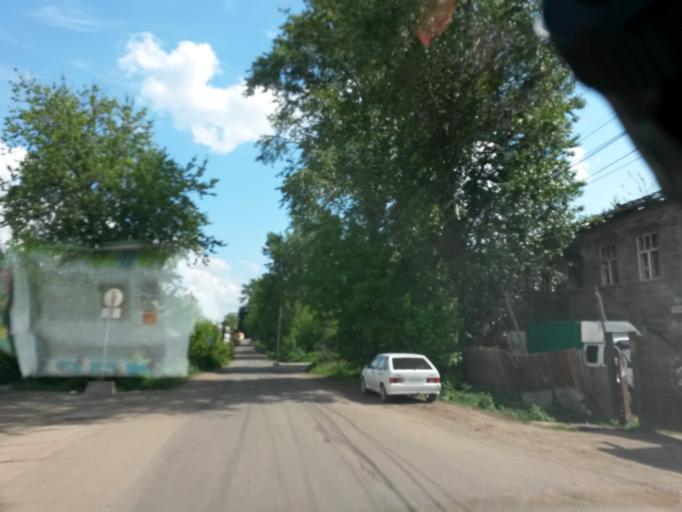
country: RU
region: Jaroslavl
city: Yaroslavl
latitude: 57.6022
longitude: 39.8921
